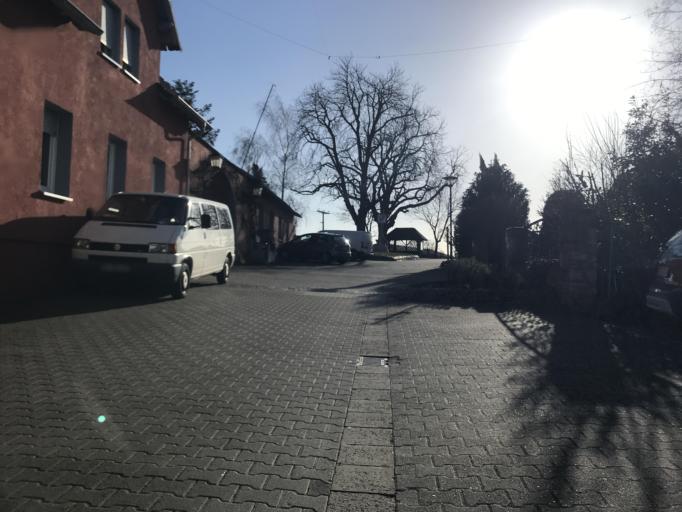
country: DE
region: Rheinland-Pfalz
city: Lorzweiler
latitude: 49.8978
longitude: 8.3009
